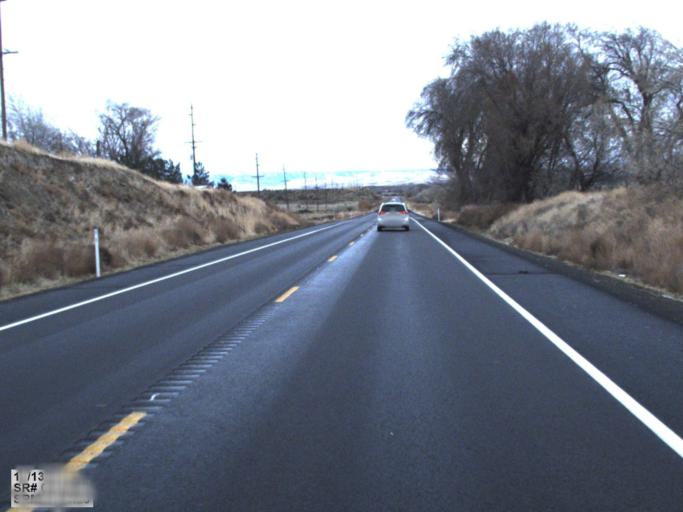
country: US
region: Washington
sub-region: Walla Walla County
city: Garrett
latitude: 46.0494
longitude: -118.7030
